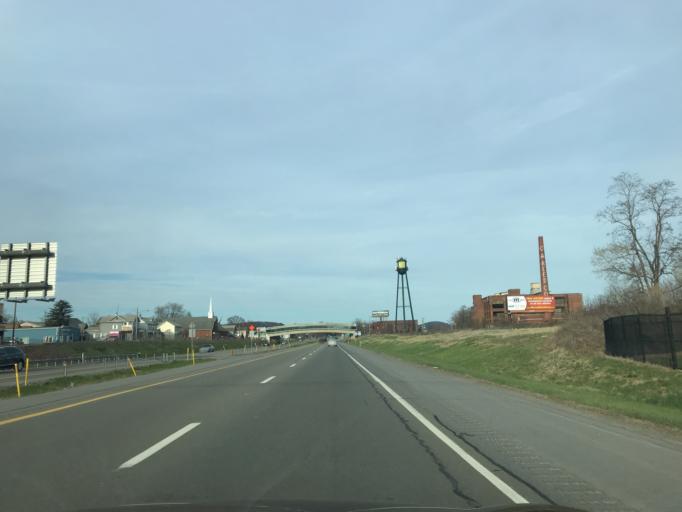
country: US
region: Pennsylvania
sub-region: Lycoming County
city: Faxon
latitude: 41.2457
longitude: -76.9888
